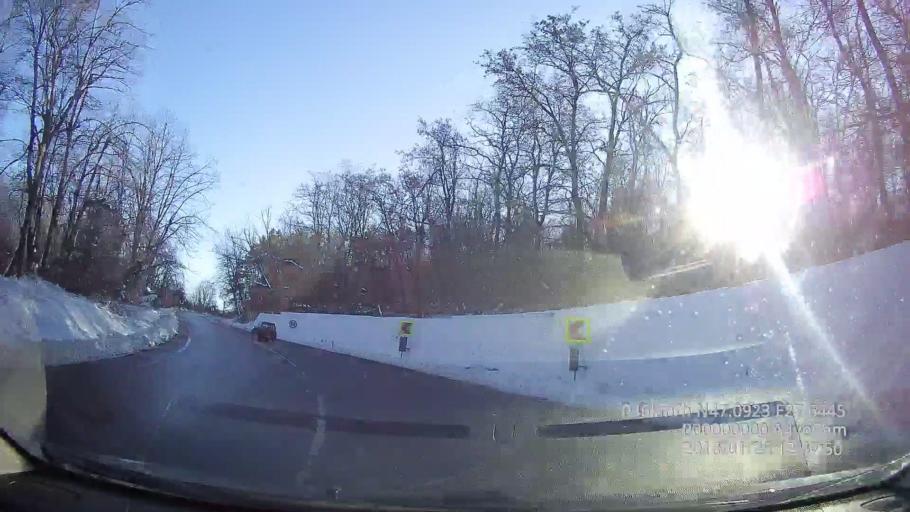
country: RO
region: Iasi
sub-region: Comuna Barnova
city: Barnova
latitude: 47.0920
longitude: 27.6449
